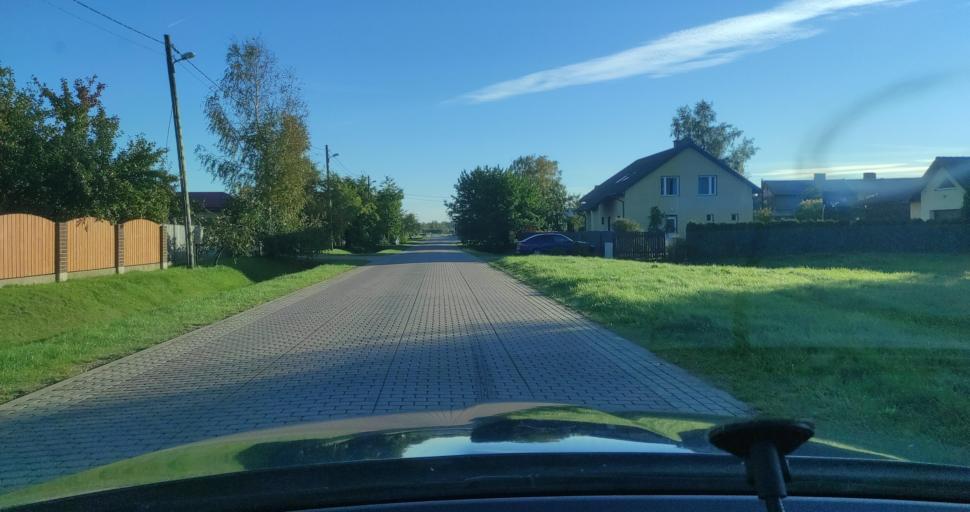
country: LV
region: Ventspils
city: Ventspils
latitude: 57.3702
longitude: 21.5755
